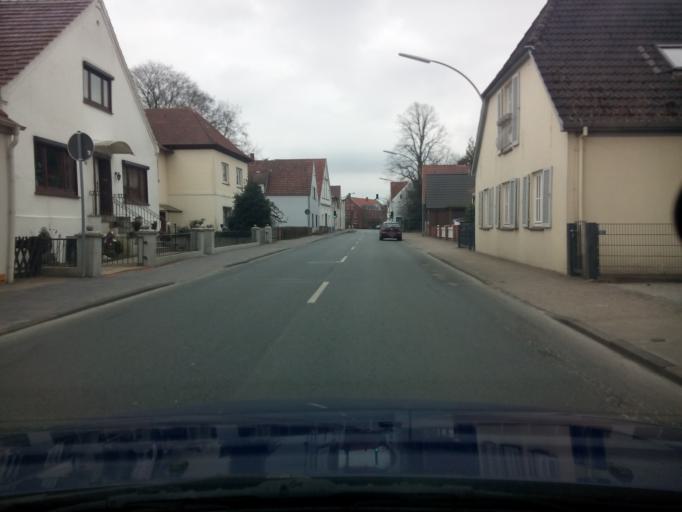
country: DE
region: Lower Saxony
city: Osterholz-Scharmbeck
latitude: 53.2270
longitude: 8.8120
